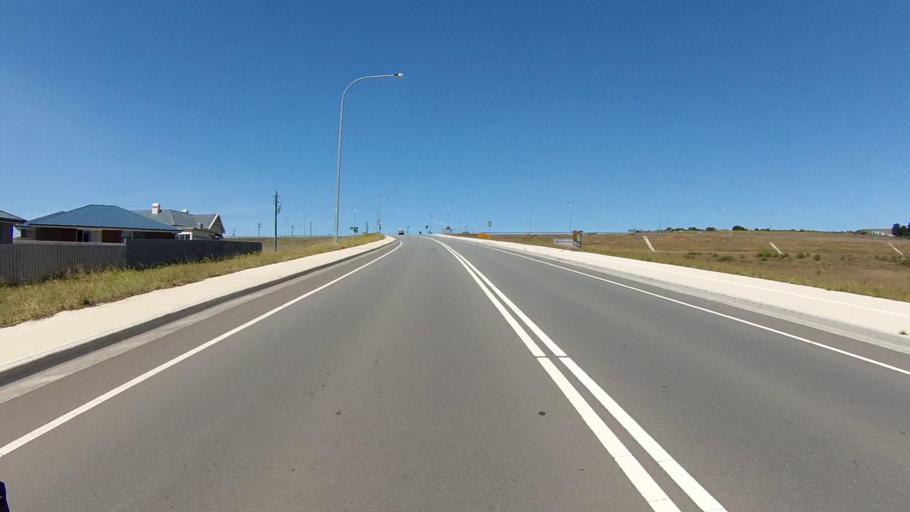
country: AU
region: Tasmania
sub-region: Clarence
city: Howrah
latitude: -42.8870
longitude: 147.4285
